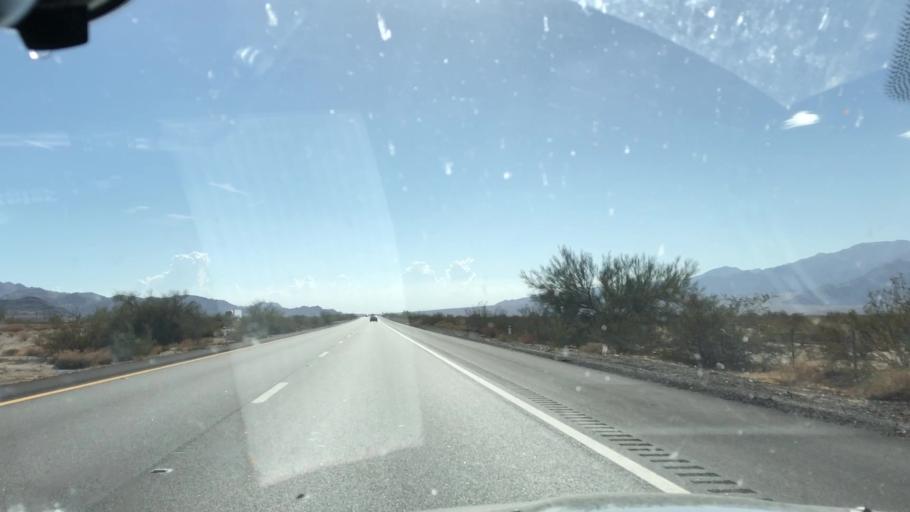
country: US
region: California
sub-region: Imperial County
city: Niland
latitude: 33.6726
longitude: -115.5981
